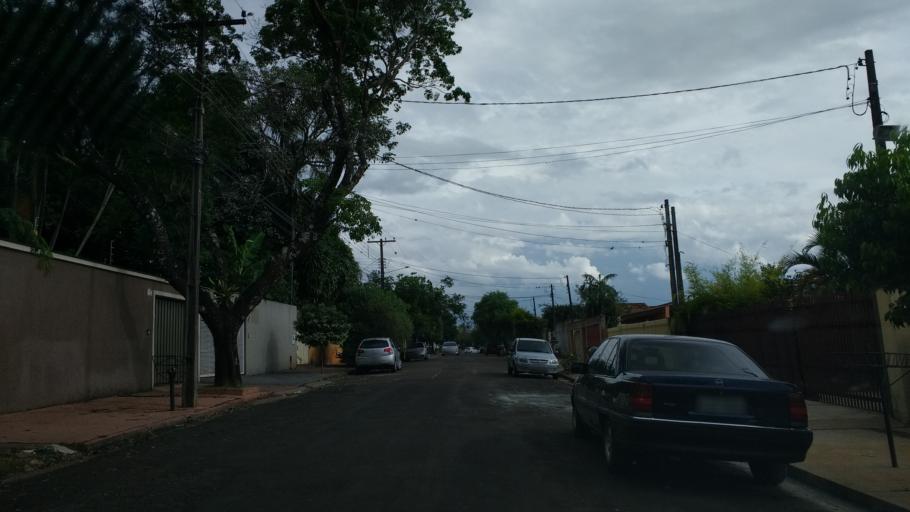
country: BR
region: Parana
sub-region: Londrina
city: Londrina
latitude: -23.3097
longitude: -51.1809
